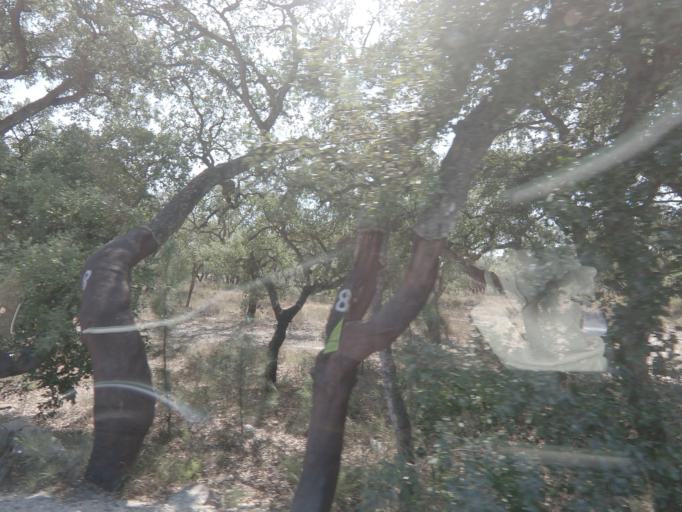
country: PT
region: Setubal
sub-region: Palmela
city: Palmela
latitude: 38.5911
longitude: -8.8534
